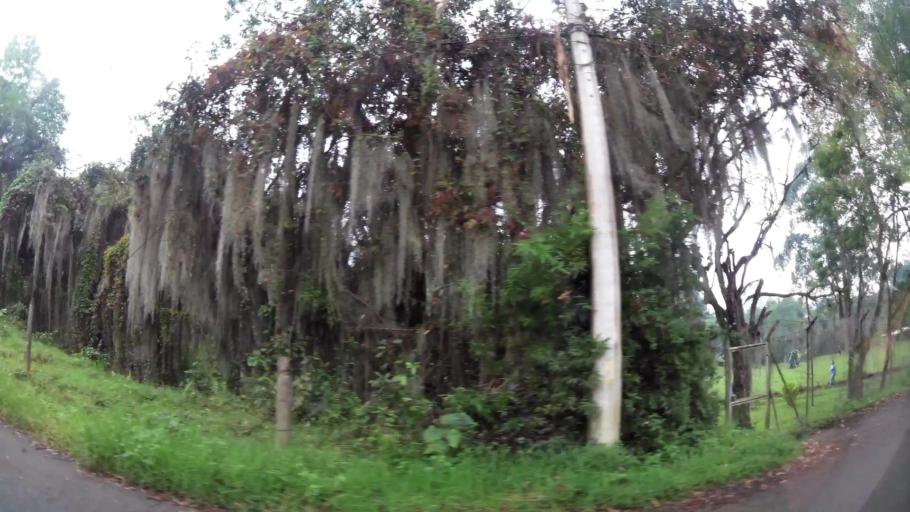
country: CO
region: Antioquia
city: Envigado
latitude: 6.1807
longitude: -75.5594
